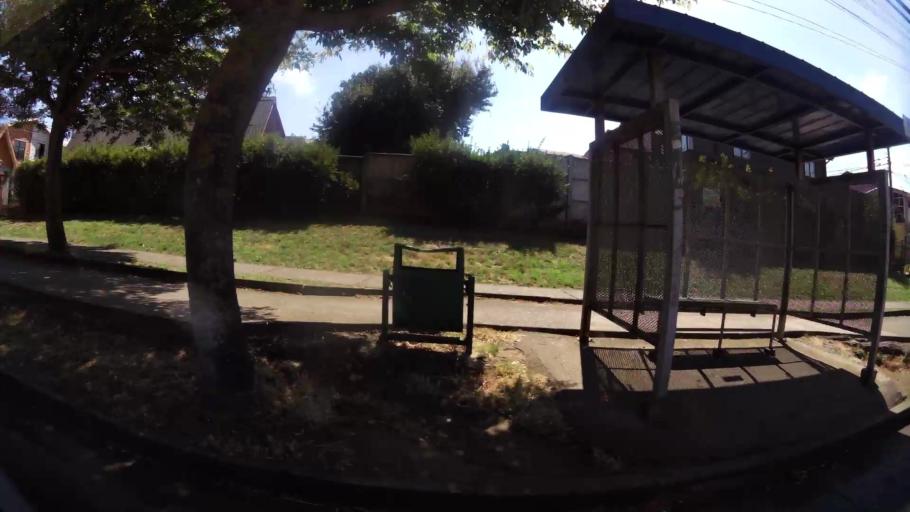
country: CL
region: Biobio
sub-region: Provincia de Concepcion
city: Concepcion
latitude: -36.7817
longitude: -73.0420
